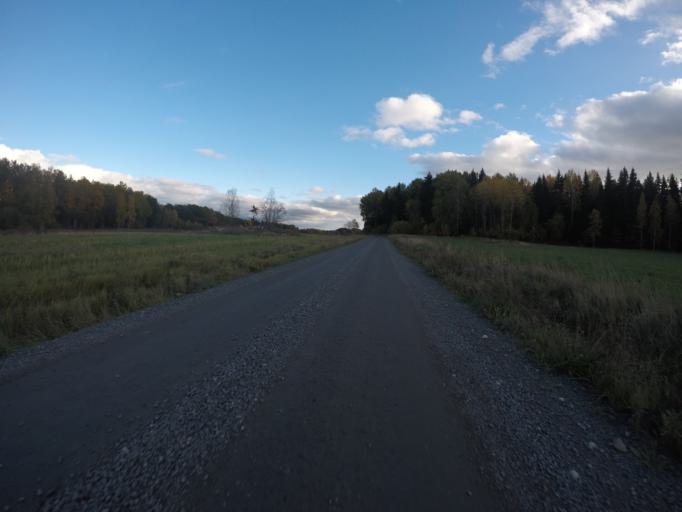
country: SE
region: Vaestmanland
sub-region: Arboga Kommun
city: Tyringe
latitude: 59.3092
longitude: 15.9766
